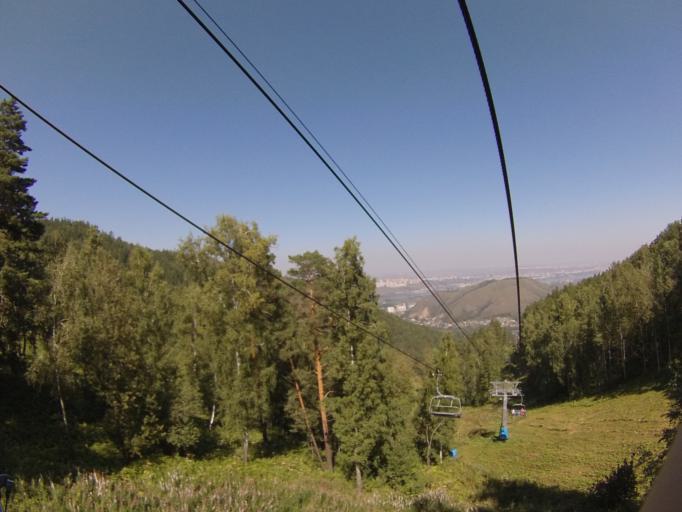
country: RU
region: Krasnoyarskiy
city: Krasnoyarsk
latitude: 55.9509
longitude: 92.7880
